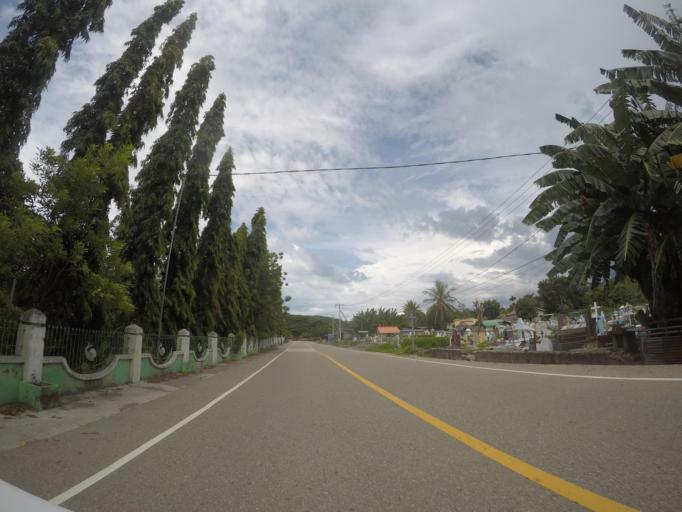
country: TL
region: Liquica
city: Maubara
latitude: -8.6117
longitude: 125.2022
